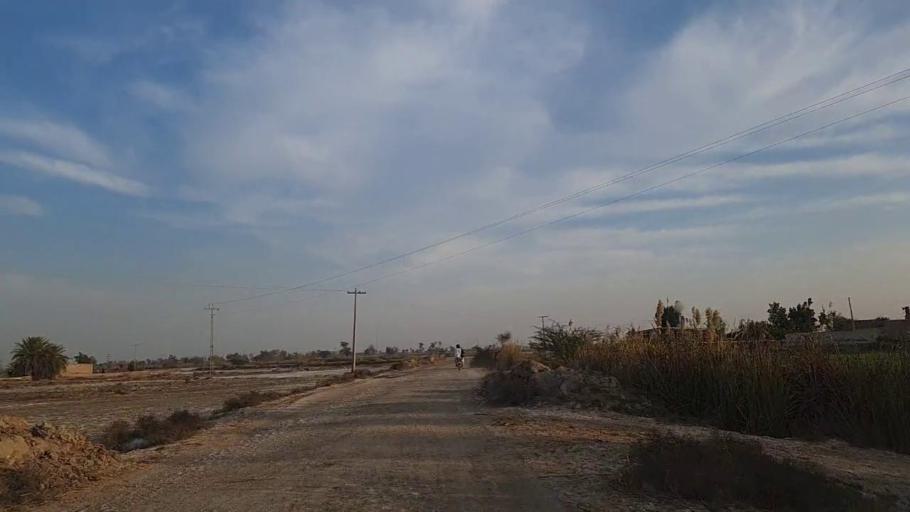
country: PK
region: Sindh
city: Bandhi
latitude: 26.5755
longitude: 68.3369
